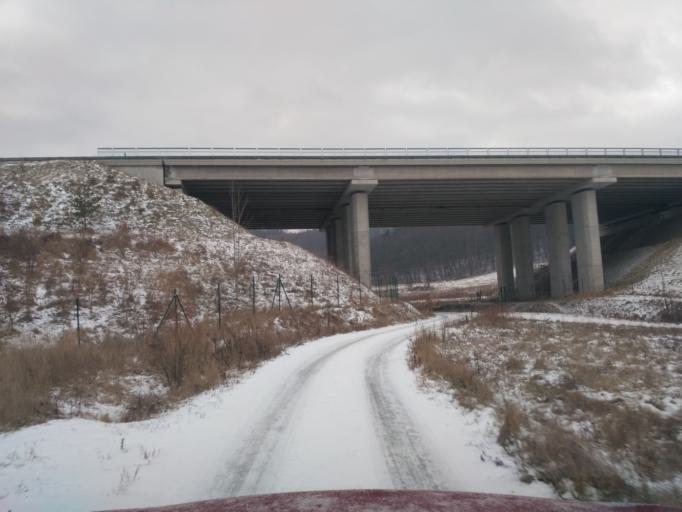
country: SK
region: Presovsky
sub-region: Okres Presov
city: Presov
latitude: 49.0034
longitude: 21.1760
